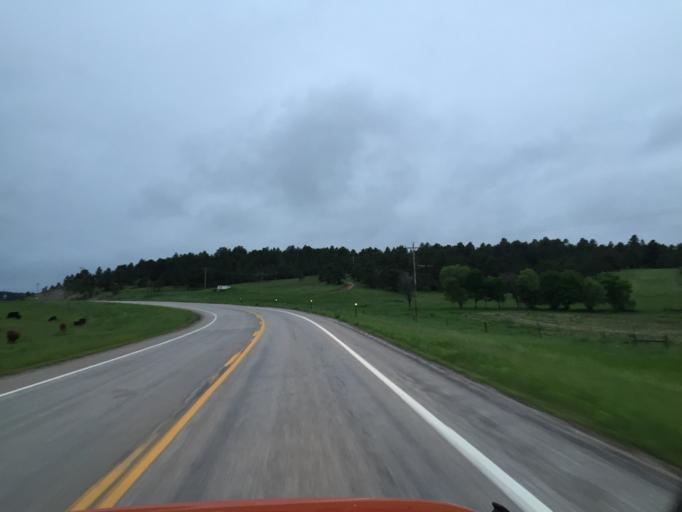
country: US
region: South Dakota
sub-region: Pennington County
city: Colonial Pine Hills
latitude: 43.8348
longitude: -103.2168
